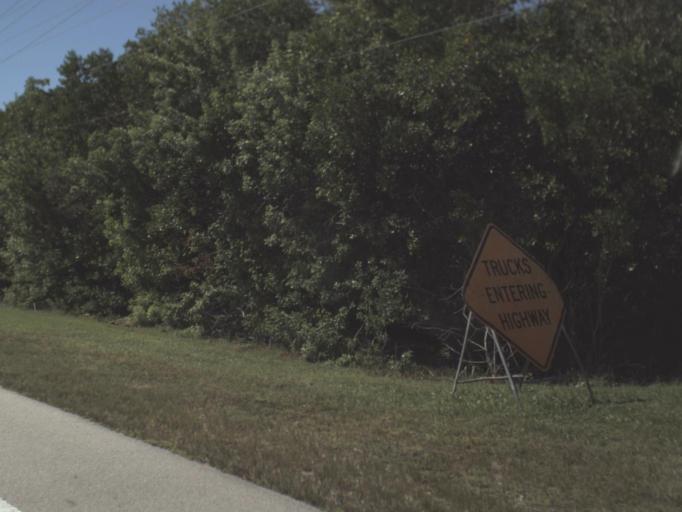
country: US
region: Florida
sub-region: Collier County
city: Marco
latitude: 25.9739
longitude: -81.7064
